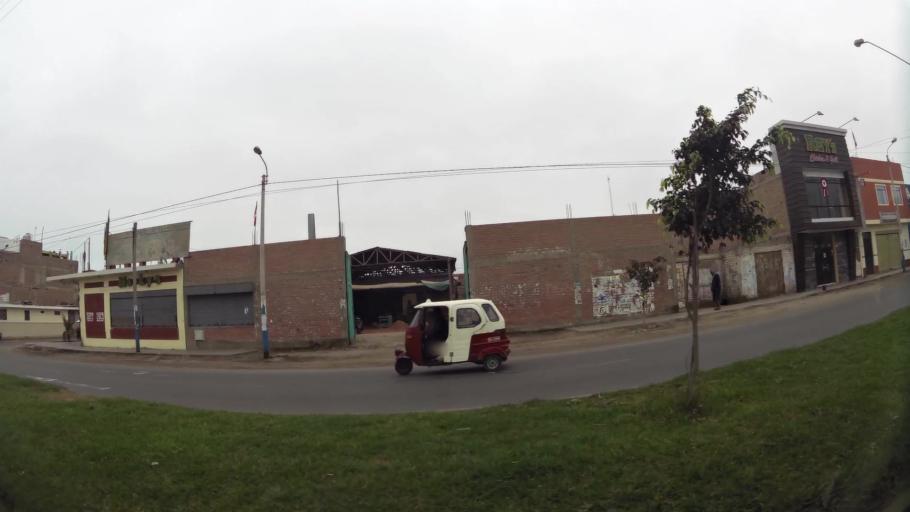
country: PE
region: Ica
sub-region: Provincia de Pisco
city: Pisco
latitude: -13.7171
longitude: -76.2067
